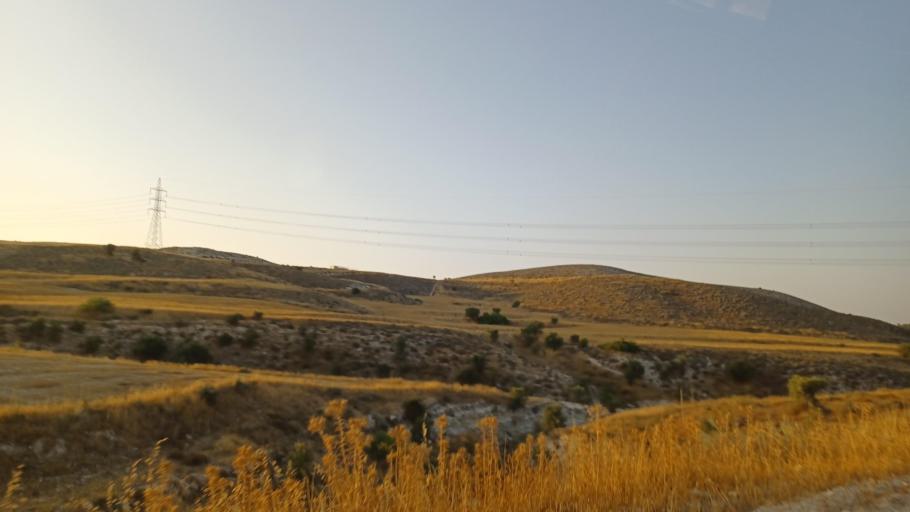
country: CY
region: Larnaka
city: Athienou
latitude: 34.9934
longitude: 33.5332
